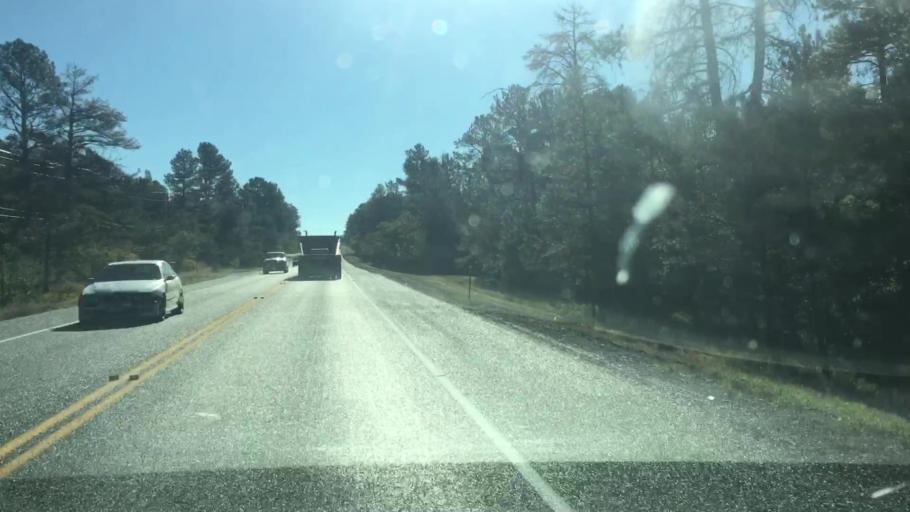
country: US
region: Colorado
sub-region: Douglas County
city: The Pinery
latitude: 39.3869
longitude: -104.7355
